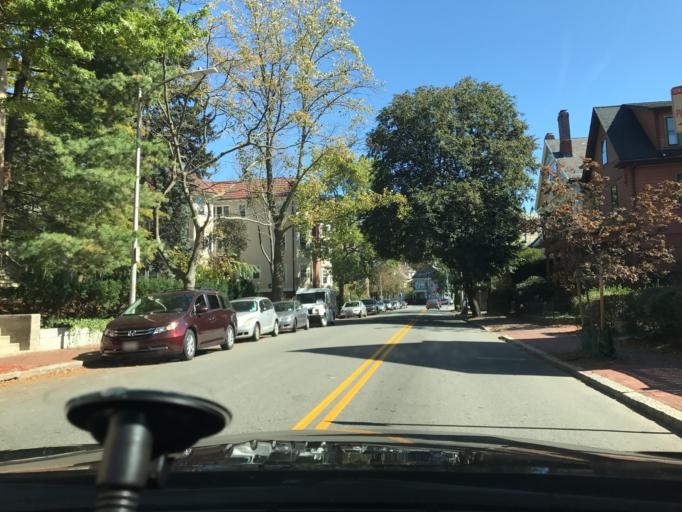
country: US
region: Massachusetts
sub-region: Middlesex County
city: Cambridge
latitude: 42.3844
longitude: -71.1211
